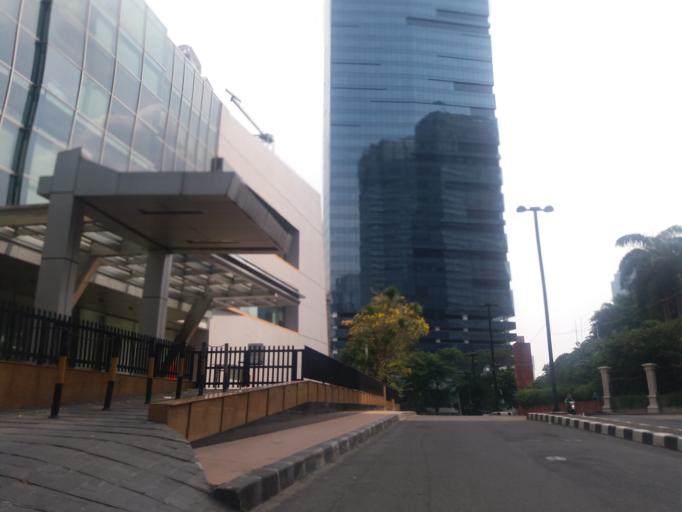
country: ID
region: Jakarta Raya
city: Jakarta
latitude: -6.2175
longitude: 106.8185
